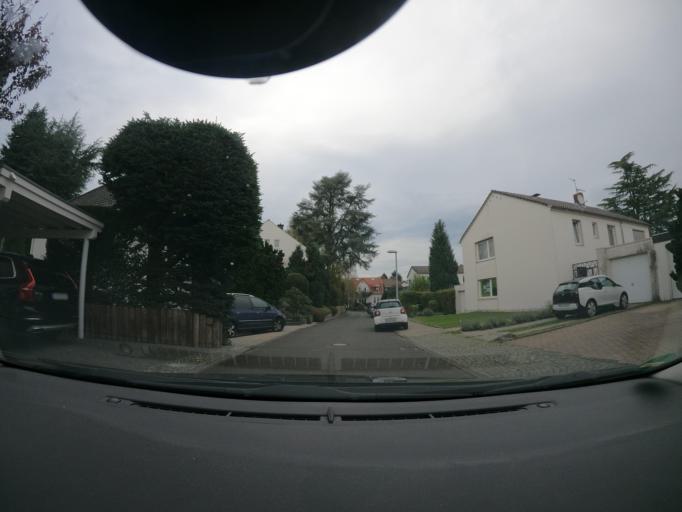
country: DE
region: North Rhine-Westphalia
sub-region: Regierungsbezirk Koln
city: Aachen
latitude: 50.7553
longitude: 6.0808
